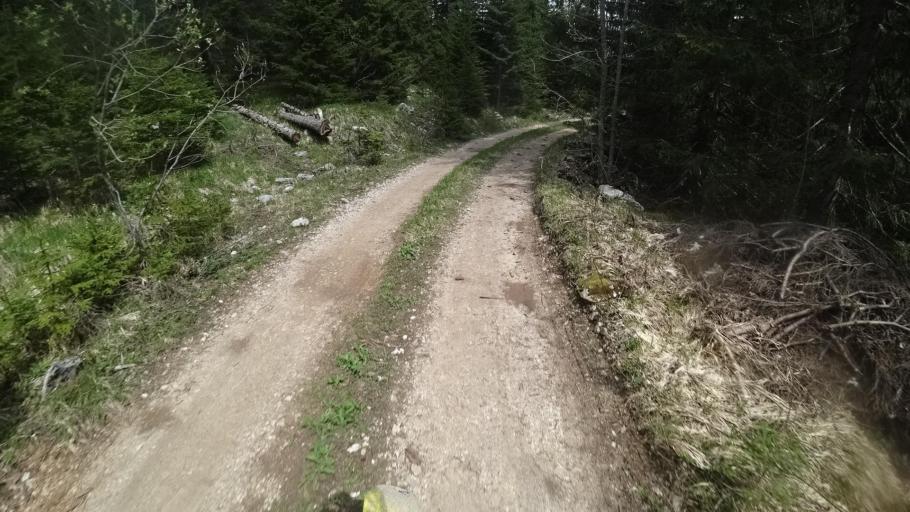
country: BA
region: Republika Srpska
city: Sipovo
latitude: 44.1248
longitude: 17.0793
